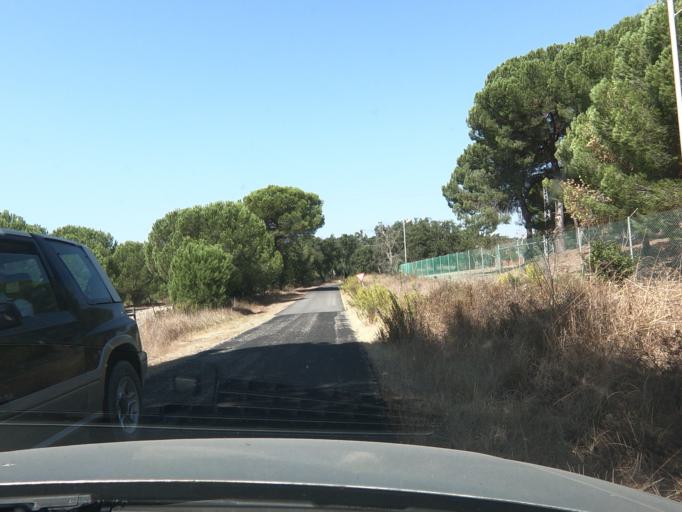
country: PT
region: Setubal
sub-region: Alcacer do Sal
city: Alcacer do Sal
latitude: 38.2658
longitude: -8.3153
